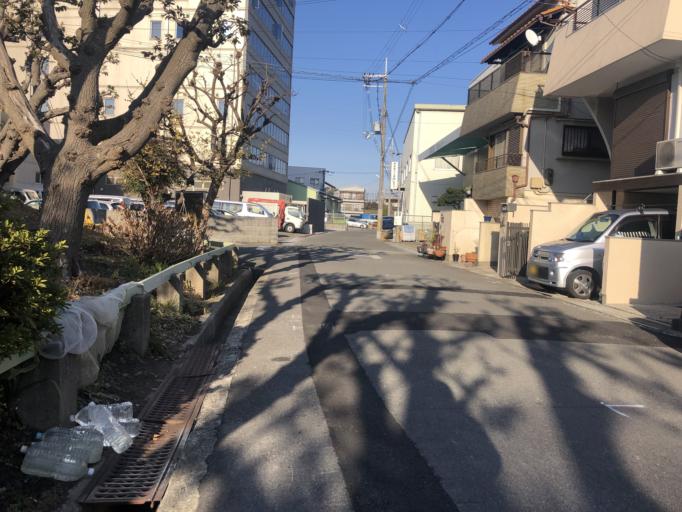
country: JP
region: Osaka
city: Suita
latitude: 34.7509
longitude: 135.5115
